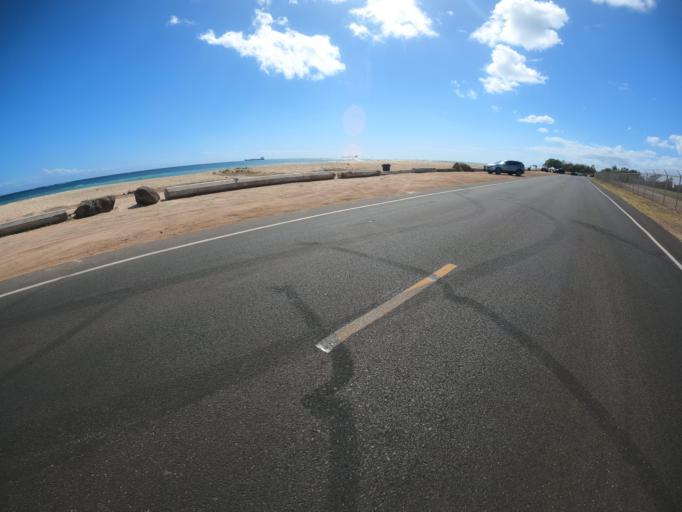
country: US
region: Hawaii
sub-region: Honolulu County
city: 'Ewa Villages
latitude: 21.3004
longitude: -158.0619
